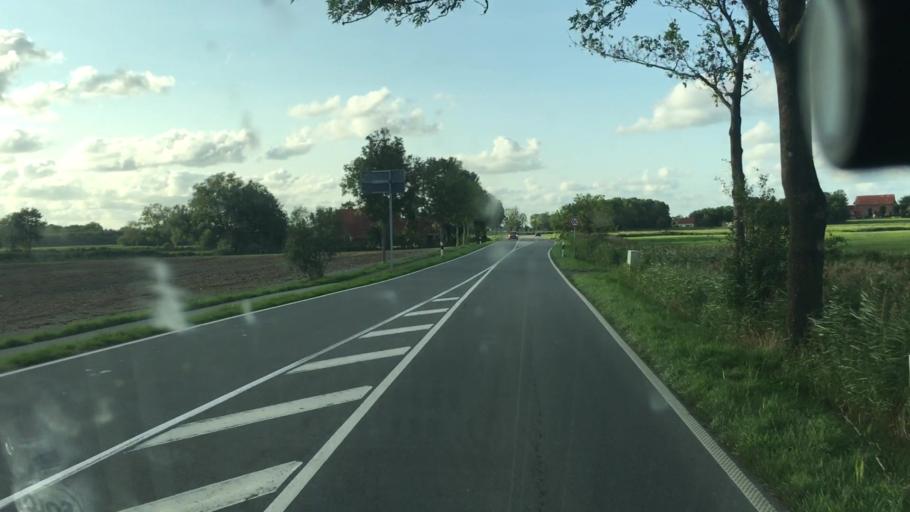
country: DE
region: Lower Saxony
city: Jever
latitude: 53.5915
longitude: 7.8724
